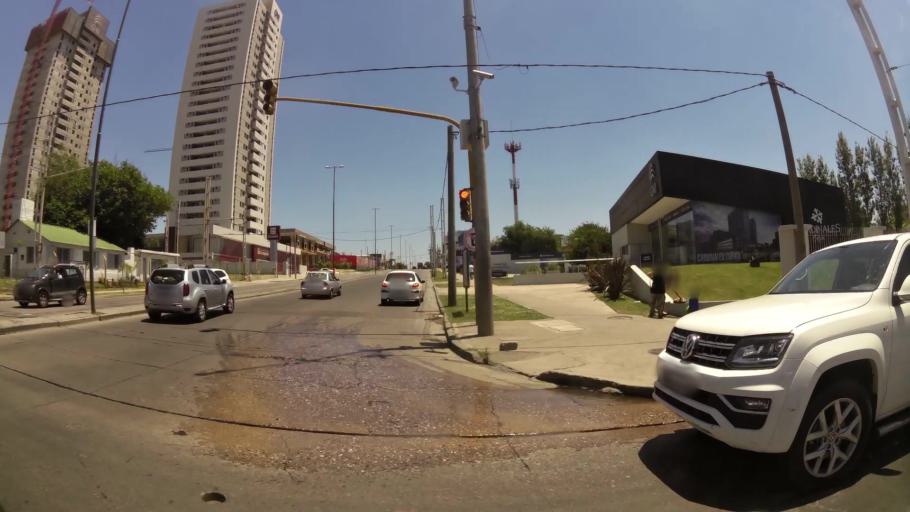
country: AR
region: Cordoba
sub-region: Departamento de Capital
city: Cordoba
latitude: -31.4007
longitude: -64.2250
